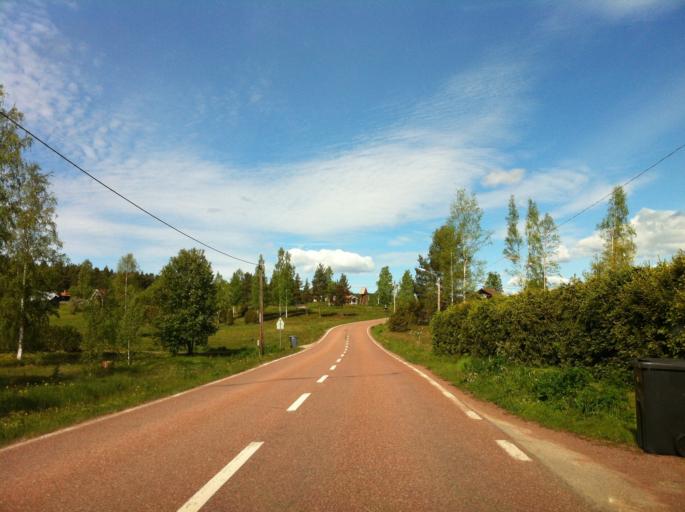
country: SE
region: Dalarna
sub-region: Mora Kommun
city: Mora
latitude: 60.8838
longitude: 14.5528
